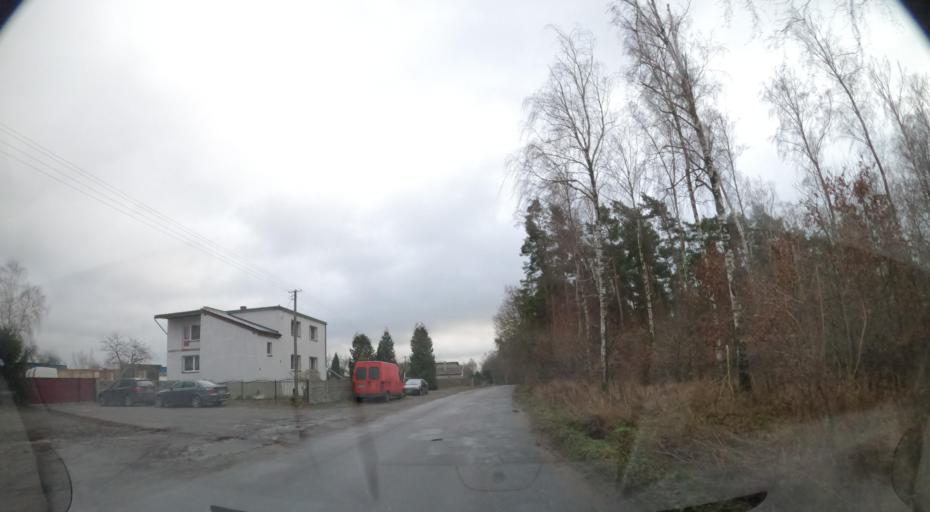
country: PL
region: Greater Poland Voivodeship
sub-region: Powiat pilski
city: Lobzenica
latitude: 53.2382
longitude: 17.3049
